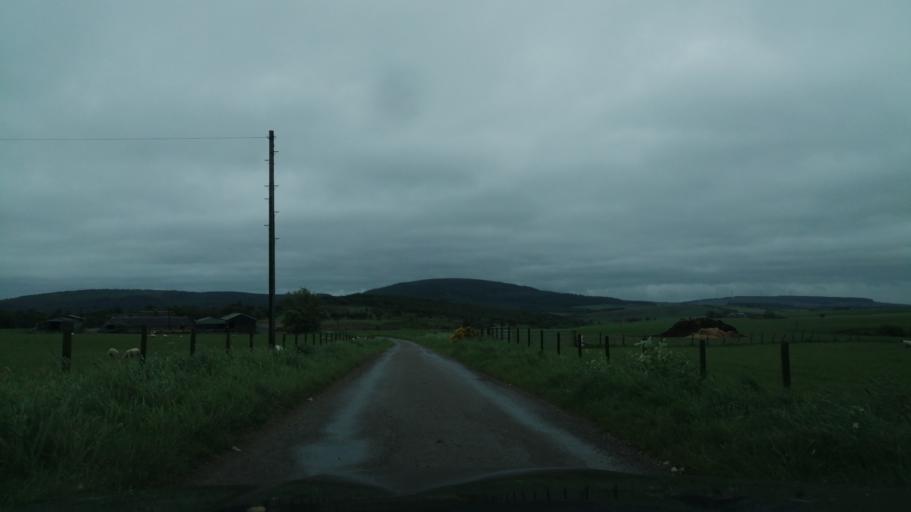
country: GB
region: Scotland
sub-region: Moray
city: Keith
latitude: 57.5743
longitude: -2.8608
